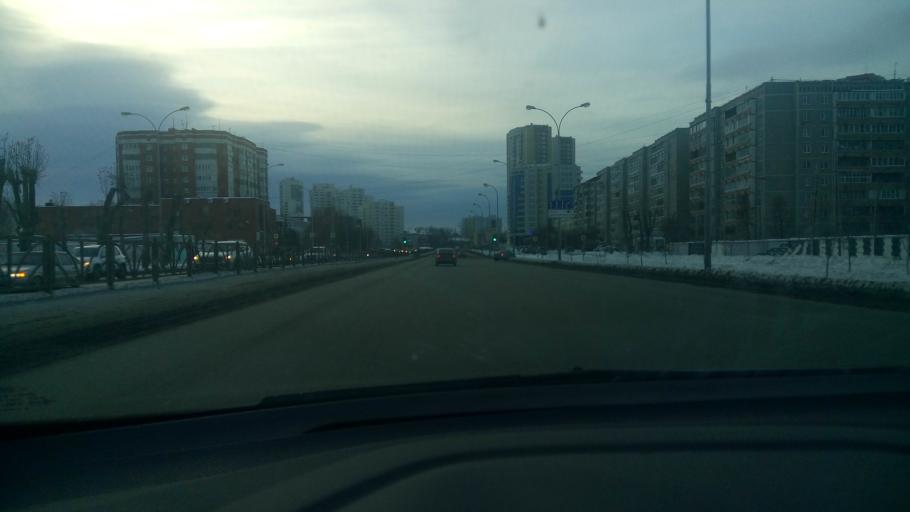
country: RU
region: Sverdlovsk
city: Yekaterinburg
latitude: 56.8089
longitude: 60.6304
